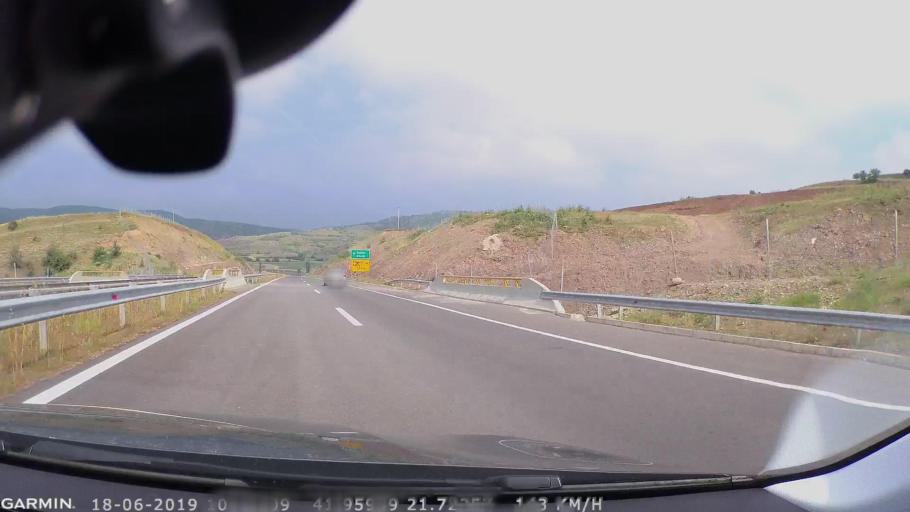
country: MK
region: Sveti Nikole
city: Gorobinci
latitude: 41.9328
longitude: 21.8262
